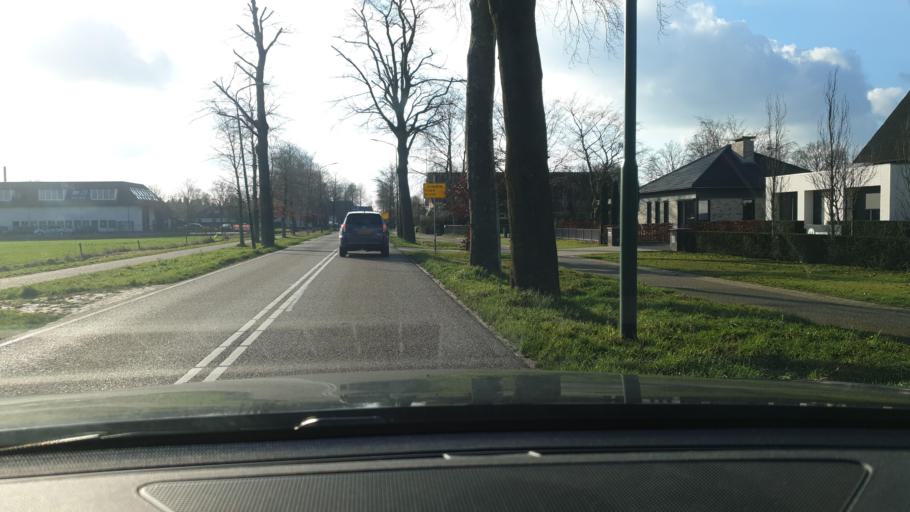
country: NL
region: North Brabant
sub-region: Bergeijk
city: Bergeyk
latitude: 51.3254
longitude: 5.3808
